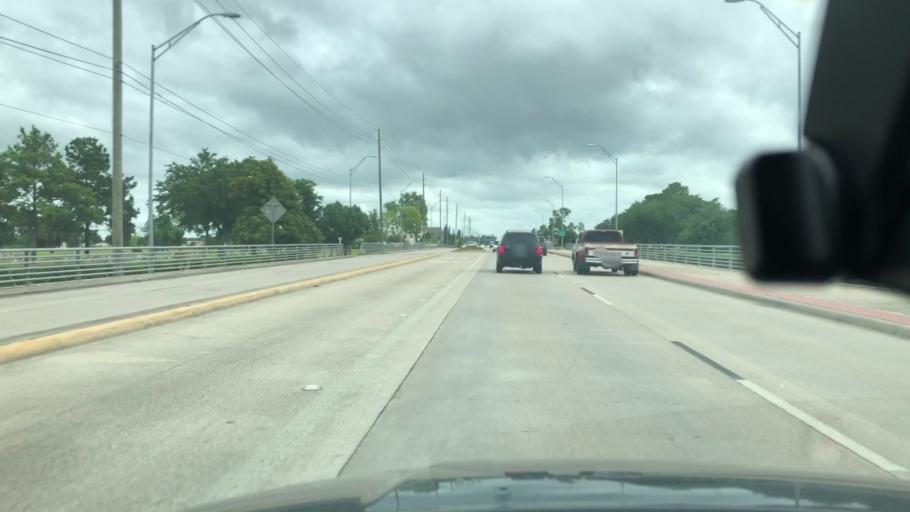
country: US
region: Texas
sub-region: Brazoria County
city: Brookside Village
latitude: 29.5678
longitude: -95.3507
